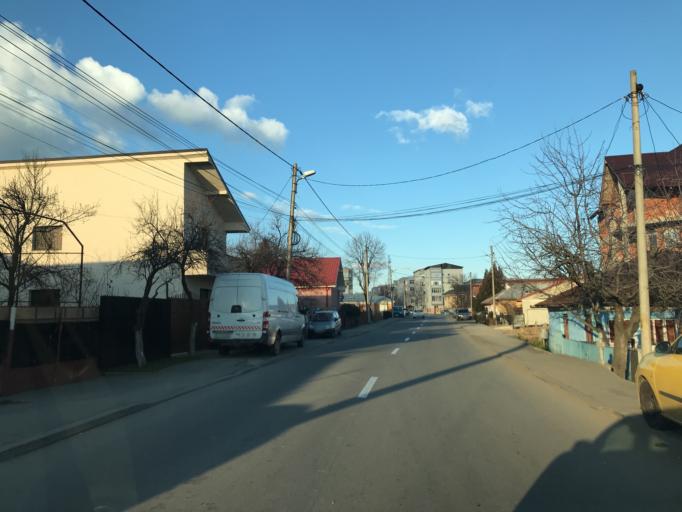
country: RO
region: Olt
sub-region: Municipiul Slatina
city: Slatina
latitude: 44.4150
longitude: 24.3795
